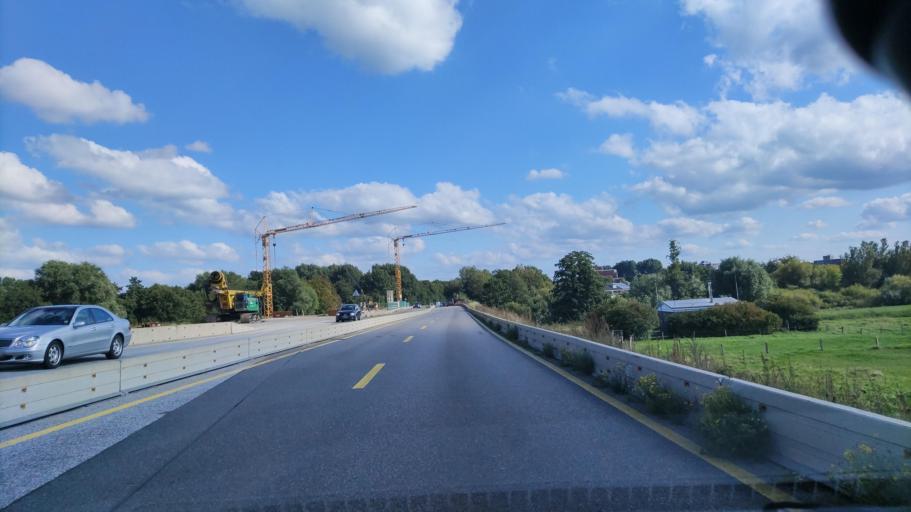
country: DE
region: Schleswig-Holstein
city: Westerronfeld
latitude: 54.3013
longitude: 9.6451
